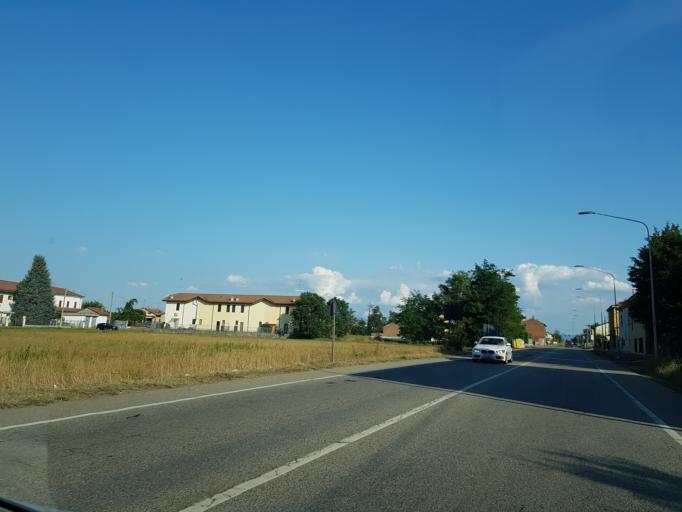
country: IT
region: Piedmont
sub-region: Provincia di Alessandria
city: Litta Parodi-Cascinagrossa
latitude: 44.8697
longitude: 8.6988
